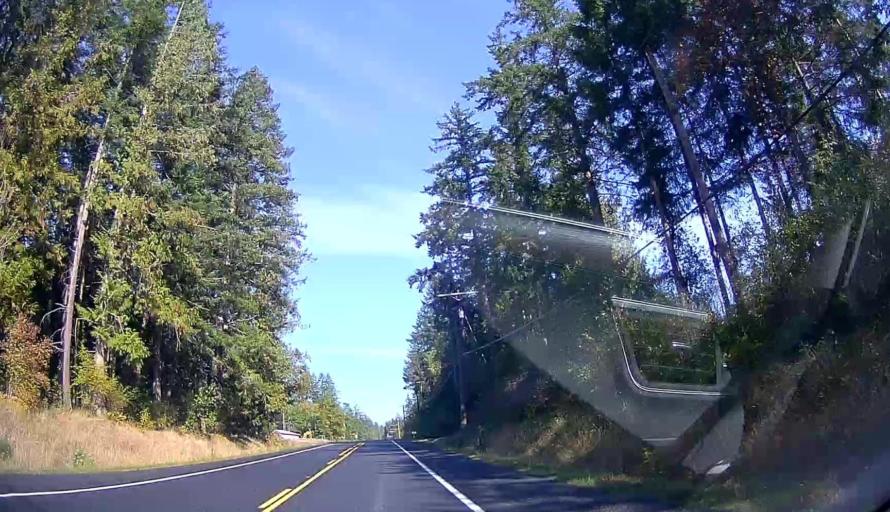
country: US
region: Washington
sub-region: Island County
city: Camano
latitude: 48.1863
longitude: -122.5103
